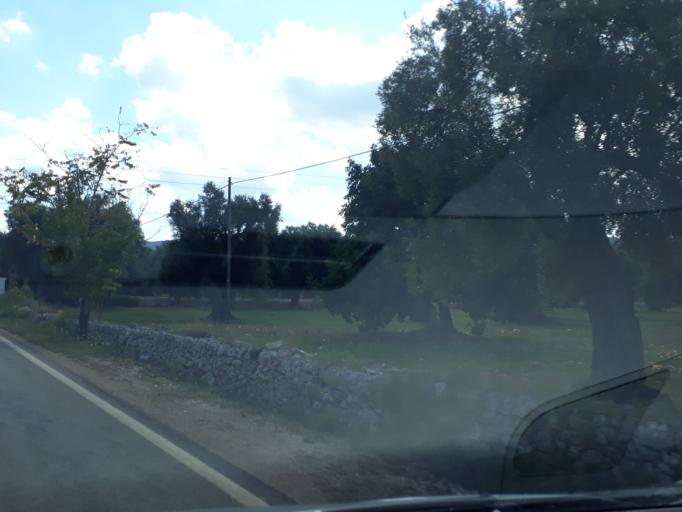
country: IT
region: Apulia
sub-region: Provincia di Brindisi
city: Fasano
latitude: 40.8153
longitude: 17.3802
